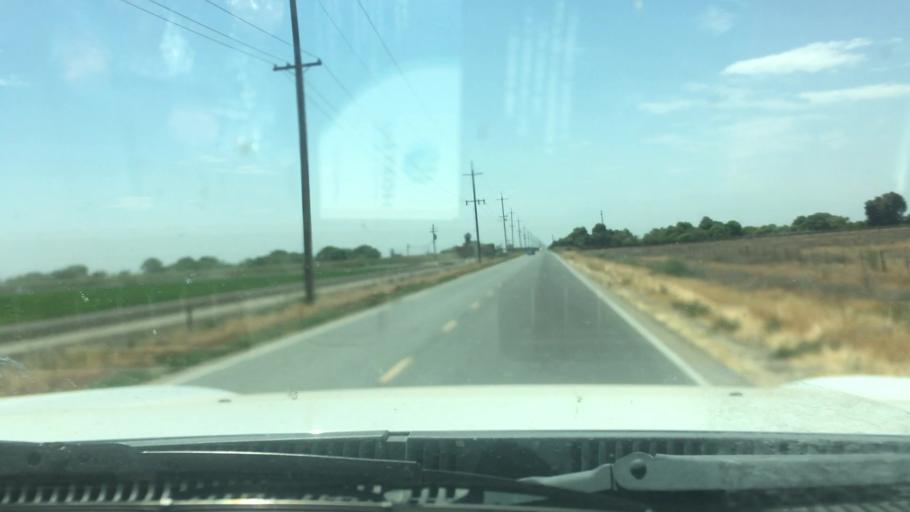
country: US
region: California
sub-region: Kings County
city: Corcoran
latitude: 36.0508
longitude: -119.4974
